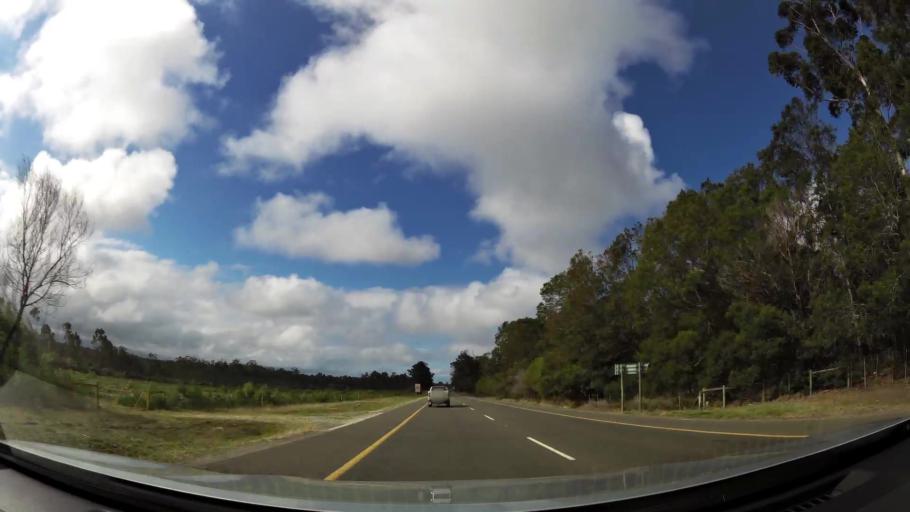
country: ZA
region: Western Cape
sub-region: Eden District Municipality
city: Plettenberg Bay
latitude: -34.0443
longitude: 23.3013
